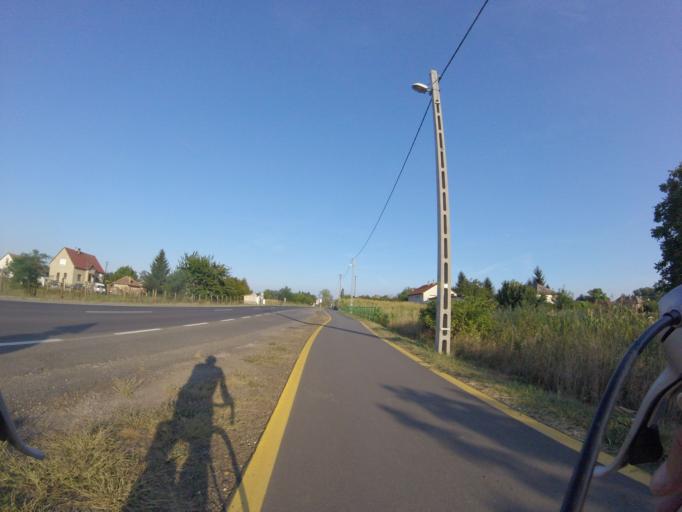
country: HU
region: Szabolcs-Szatmar-Bereg
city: Tiszanagyfalu
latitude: 48.0653
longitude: 21.5361
